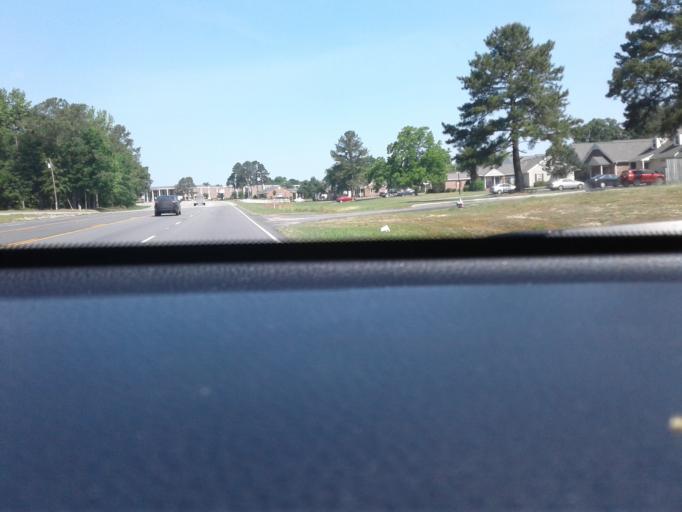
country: US
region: North Carolina
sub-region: Harnett County
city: Buies Creek
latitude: 35.4022
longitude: -78.7368
